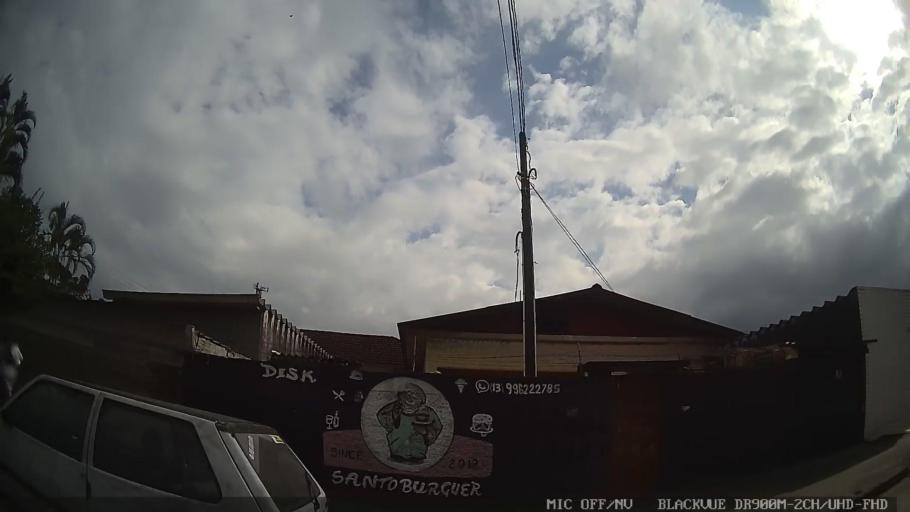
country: BR
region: Sao Paulo
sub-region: Guaruja
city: Guaruja
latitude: -23.9906
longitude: -46.2731
